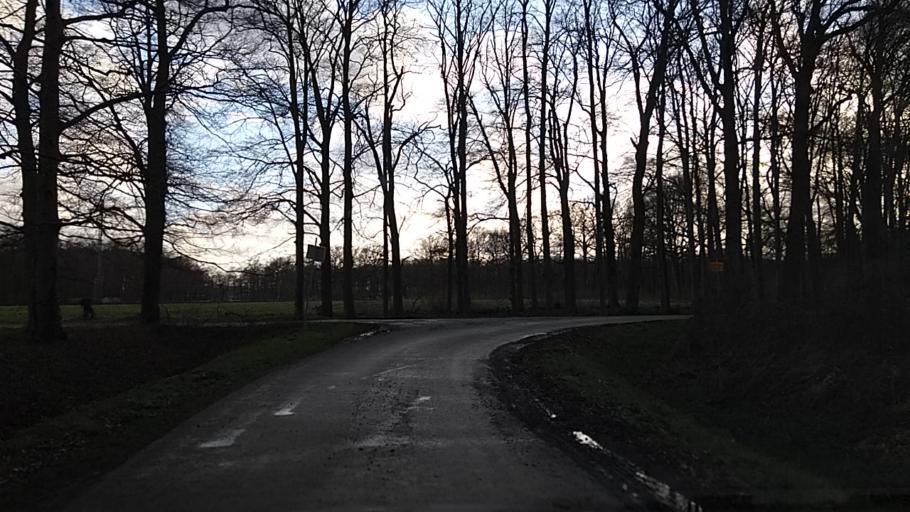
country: NL
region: Overijssel
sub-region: Gemeente Deventer
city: Schalkhaar
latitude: 52.2537
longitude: 6.2513
